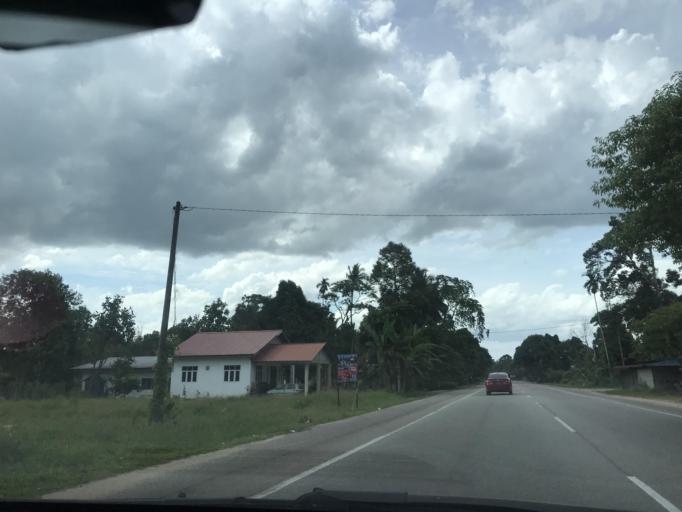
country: MY
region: Kelantan
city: Kampong Pangkal Kalong
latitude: 5.9338
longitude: 102.1914
